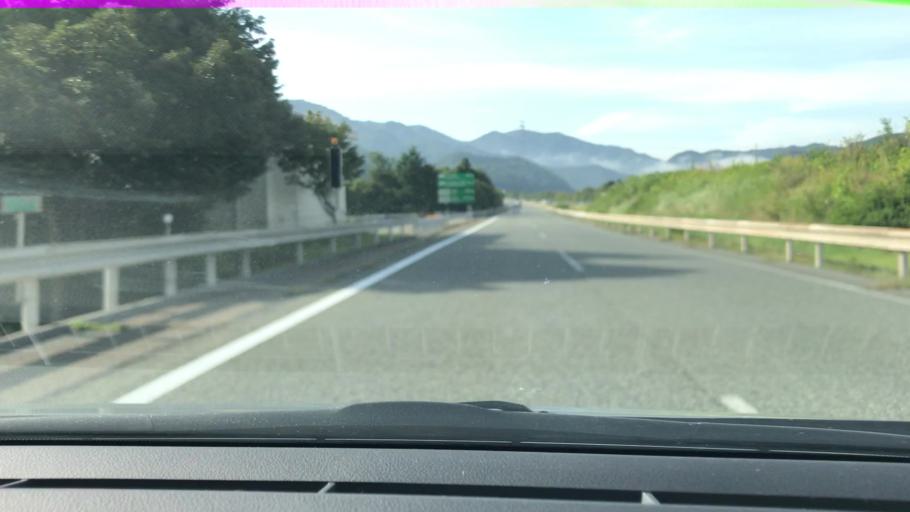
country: JP
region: Hyogo
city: Sasayama
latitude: 35.0529
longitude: 135.1838
